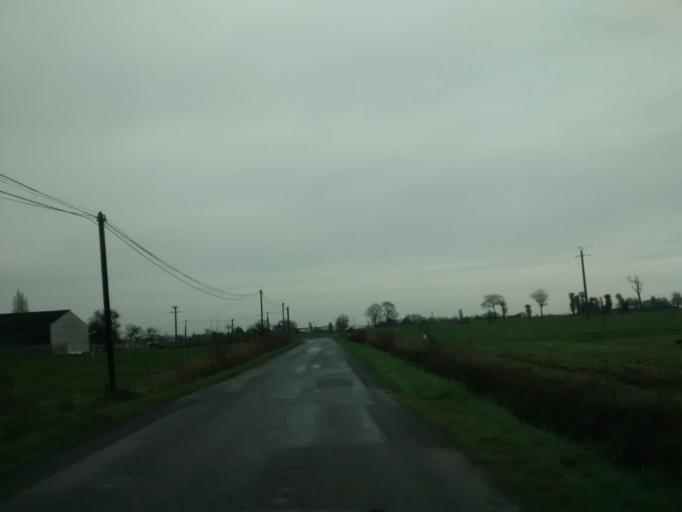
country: FR
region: Brittany
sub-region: Departement d'Ille-et-Vilaine
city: Noyal-sur-Vilaine
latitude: 48.1066
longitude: -1.5423
